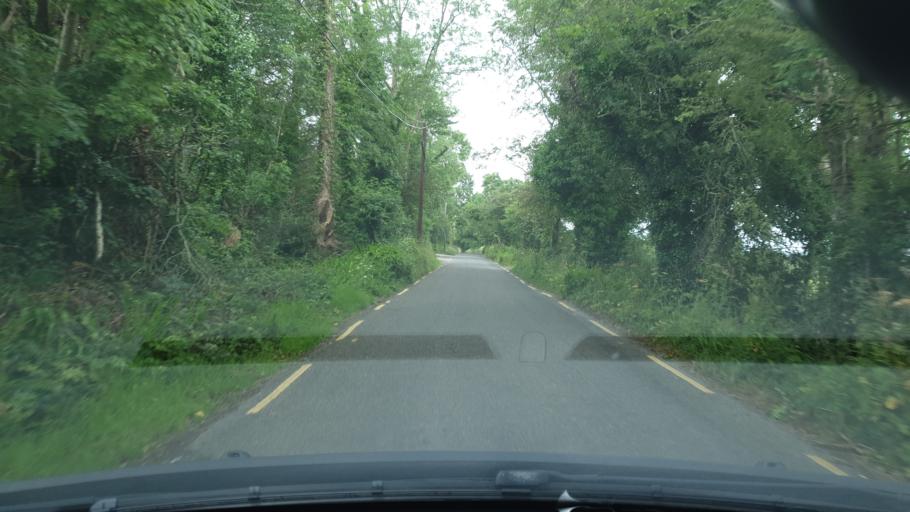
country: IE
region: Munster
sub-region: Ciarrai
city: Tralee
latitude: 52.2424
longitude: -9.6515
